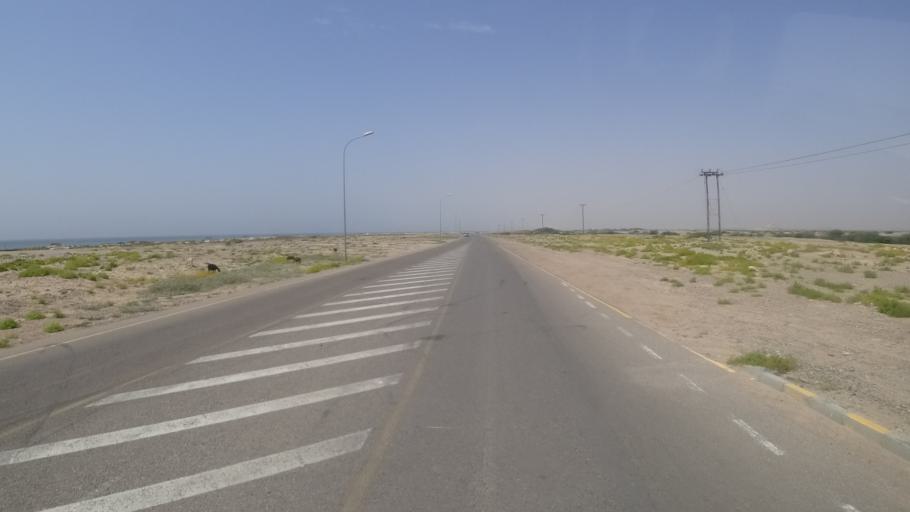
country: OM
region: Ash Sharqiyah
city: Sur
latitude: 22.1082
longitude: 59.7081
